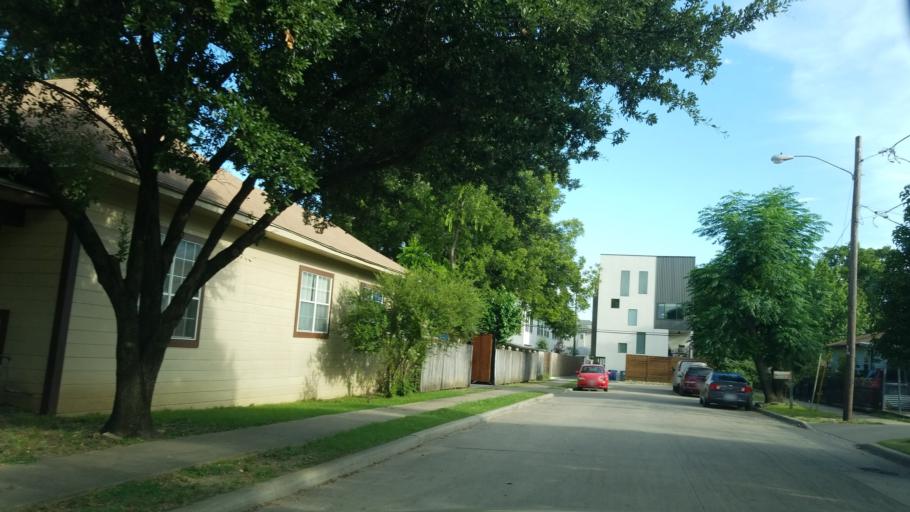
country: US
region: Texas
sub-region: Dallas County
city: Highland Park
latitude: 32.8100
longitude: -96.7677
